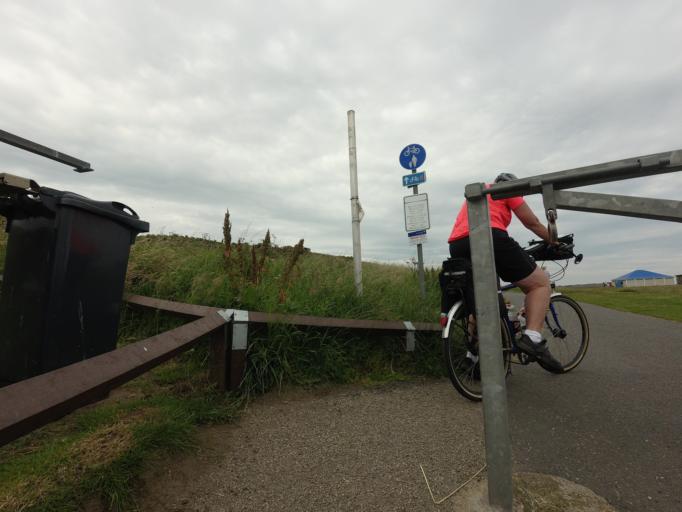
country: GB
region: Scotland
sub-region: Aberdeenshire
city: Banff
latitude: 57.6693
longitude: -2.5432
